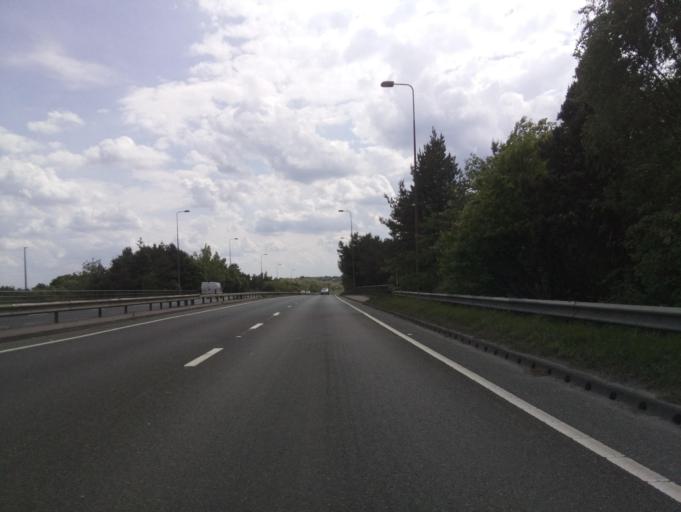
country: GB
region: England
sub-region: County Durham
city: Peterlee
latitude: 54.7646
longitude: -1.3570
